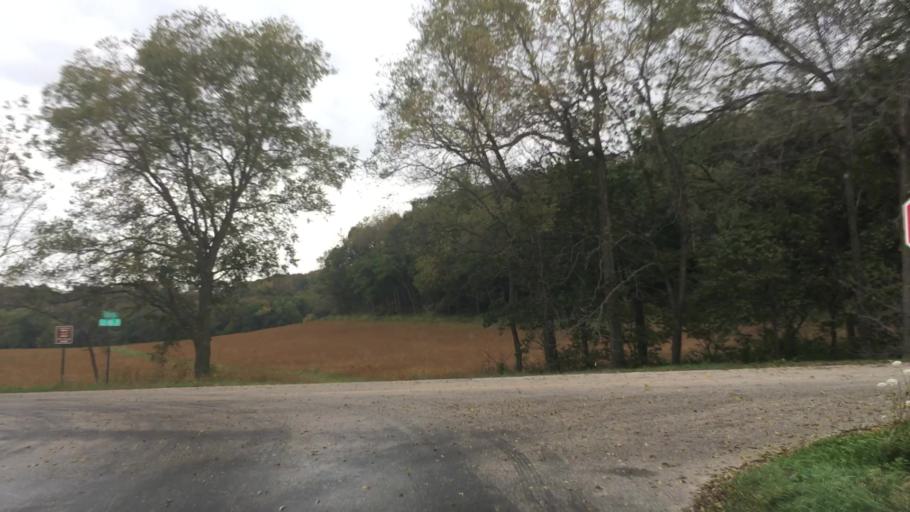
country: US
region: Minnesota
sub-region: Fillmore County
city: Preston
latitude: 43.7444
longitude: -92.0224
